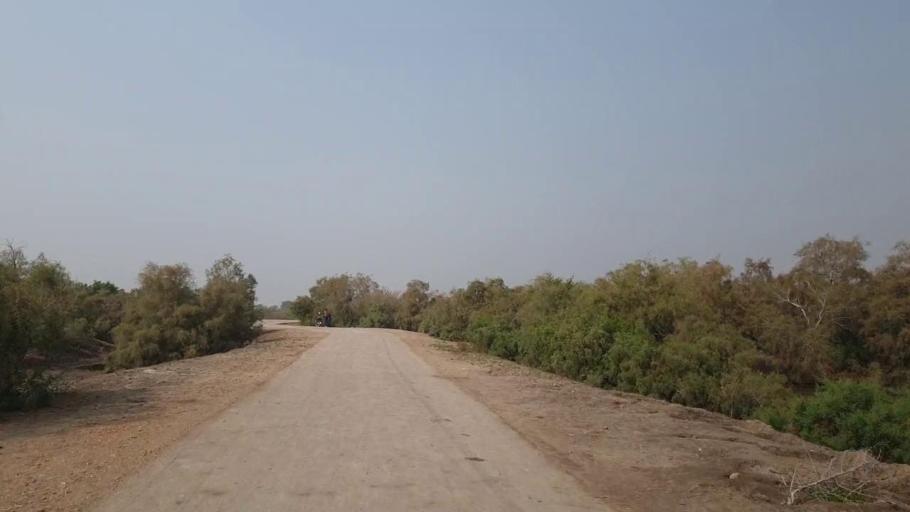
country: PK
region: Sindh
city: Bhan
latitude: 26.4895
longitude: 67.7012
